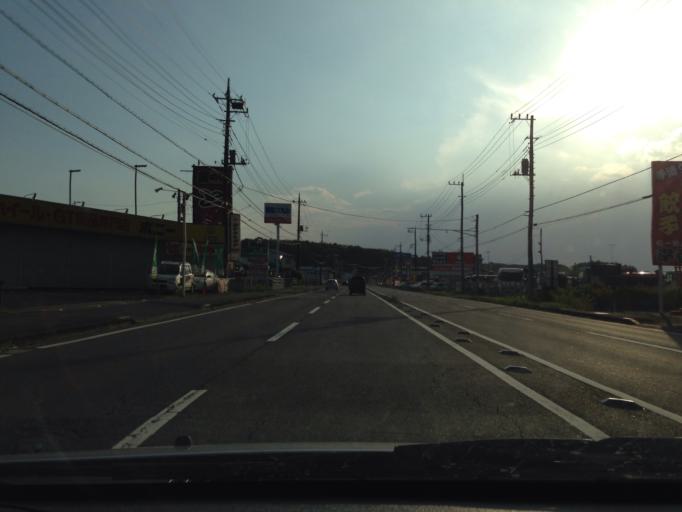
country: JP
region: Ibaraki
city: Naka
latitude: 36.0850
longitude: 140.1701
